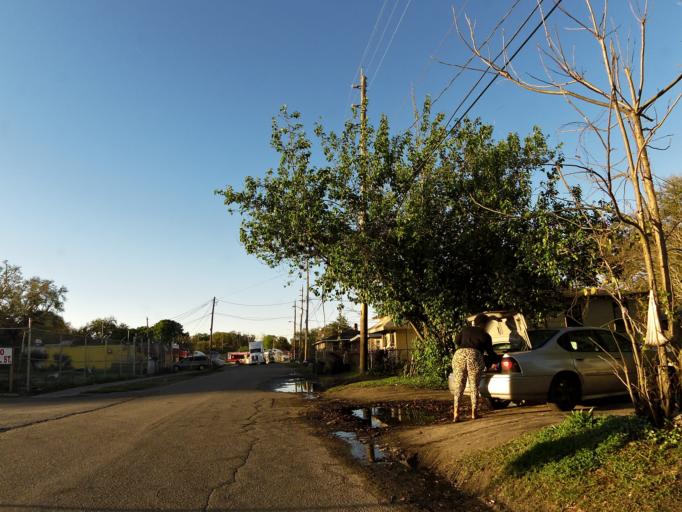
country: US
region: Florida
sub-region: Duval County
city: Jacksonville
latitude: 30.3355
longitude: -81.6986
